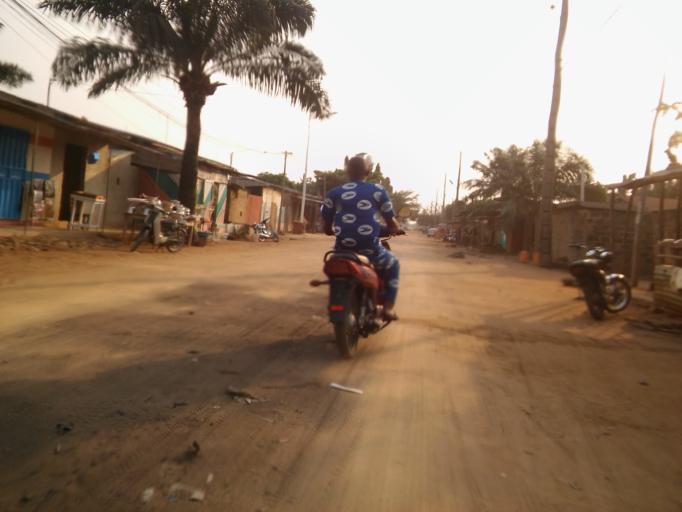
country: BJ
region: Atlantique
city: Abomey-Calavi
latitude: 6.4049
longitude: 2.3302
